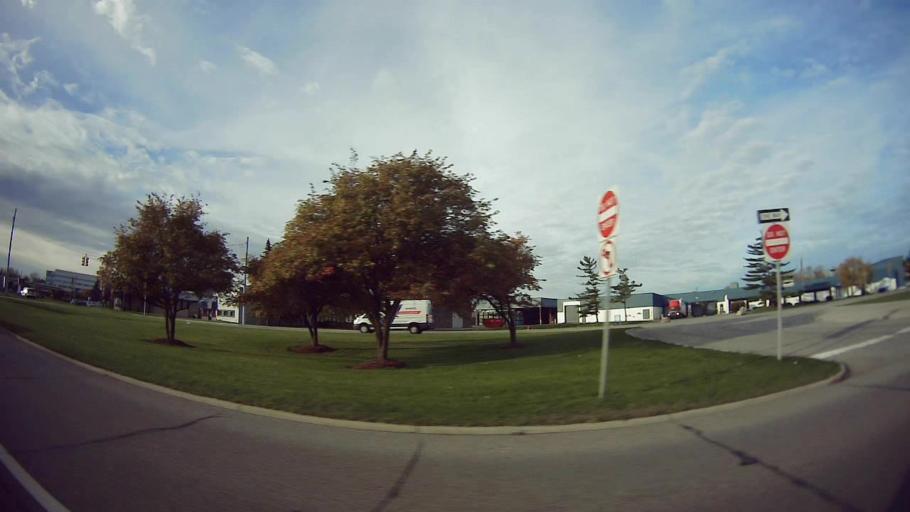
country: US
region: Michigan
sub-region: Oakland County
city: Clawson
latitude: 42.5508
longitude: -83.1230
